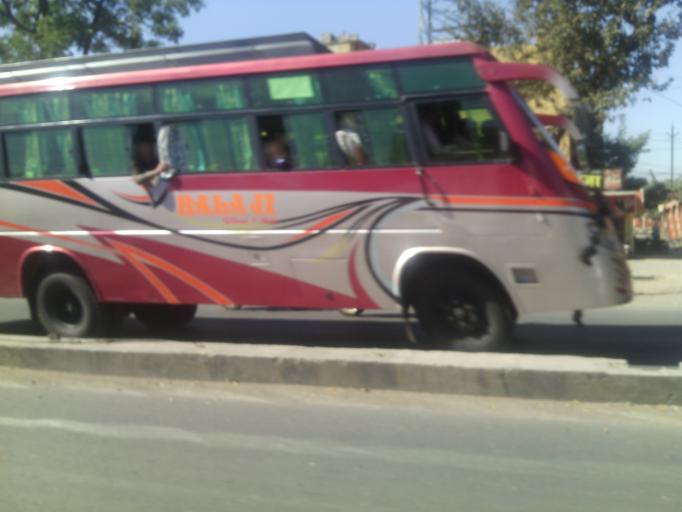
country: IN
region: Madhya Pradesh
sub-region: Dewas
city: Dewas
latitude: 22.9603
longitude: 76.0445
